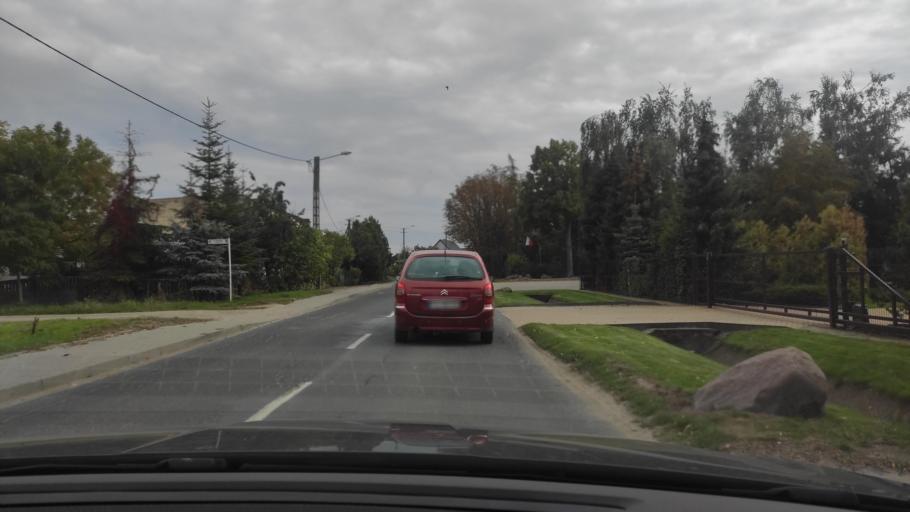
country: PL
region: Greater Poland Voivodeship
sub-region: Powiat poznanski
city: Kleszczewo
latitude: 52.3801
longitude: 17.1641
